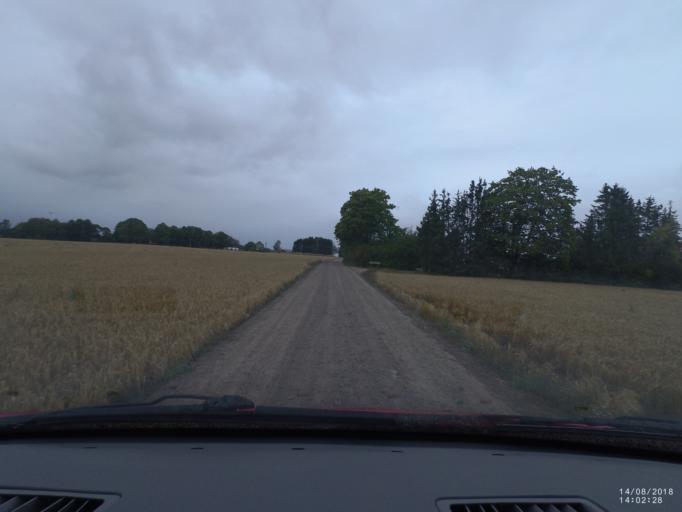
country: SE
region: Soedermanland
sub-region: Nykopings Kommun
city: Nykoping
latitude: 58.7514
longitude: 16.9693
